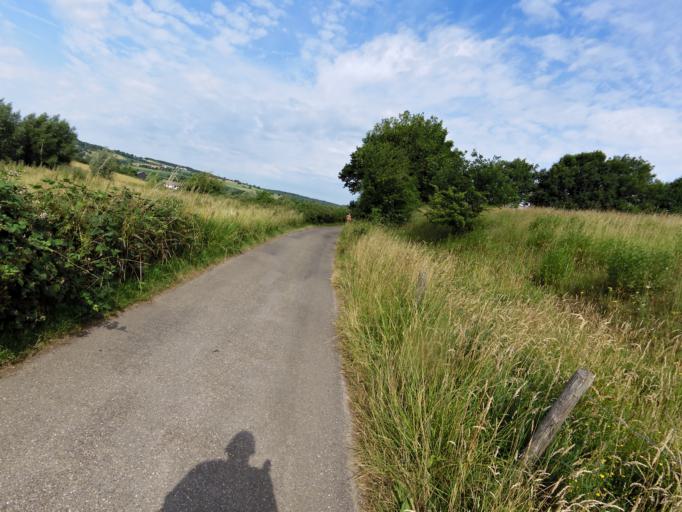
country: BE
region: Wallonia
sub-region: Province de Liege
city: Plombieres
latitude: 50.7828
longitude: 5.9303
